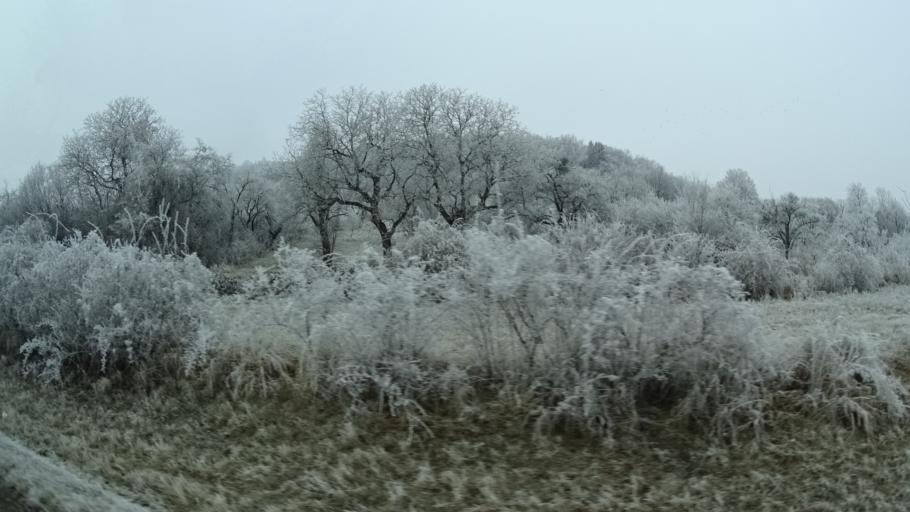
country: DE
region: Bavaria
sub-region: Regierungsbezirk Unterfranken
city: Oberelsbach
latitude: 50.4161
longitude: 10.0727
